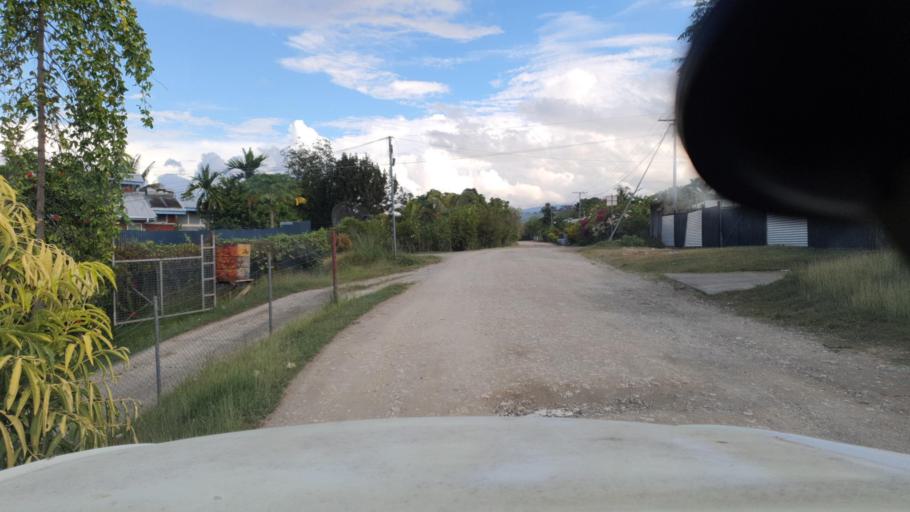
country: SB
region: Guadalcanal
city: Honiara
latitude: -9.4362
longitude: 159.9355
